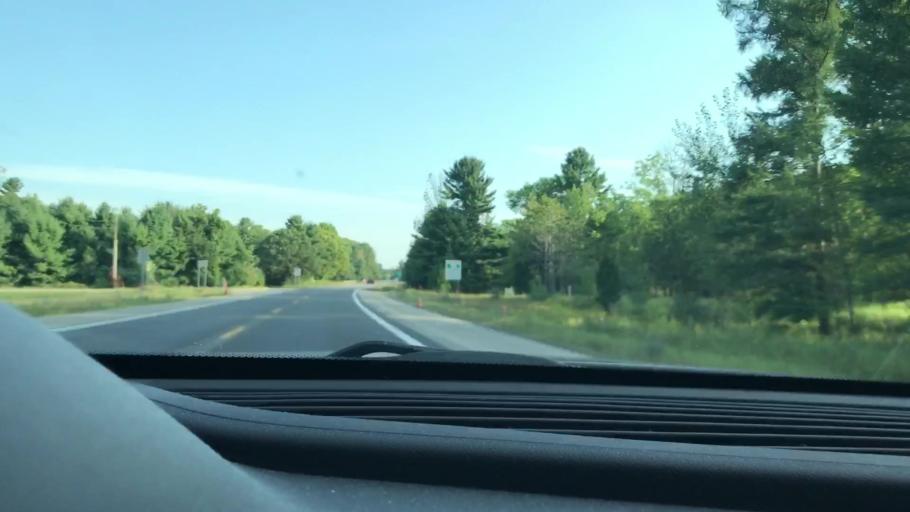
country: US
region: Michigan
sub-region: Antrim County
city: Bellaire
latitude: 45.1206
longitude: -85.3503
